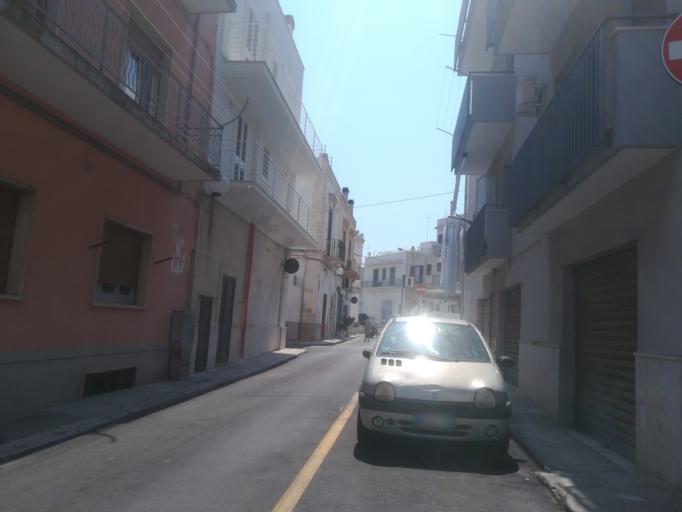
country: IT
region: Apulia
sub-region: Provincia di Bari
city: Polignano a Mare
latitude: 40.9973
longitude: 17.2154
